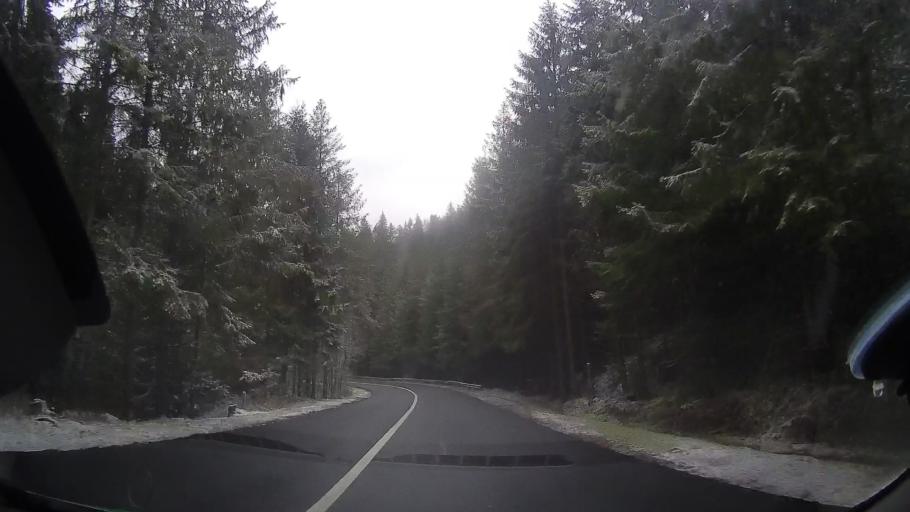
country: RO
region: Cluj
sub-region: Comuna Calatele
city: Calatele
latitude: 46.7349
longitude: 23.0388
